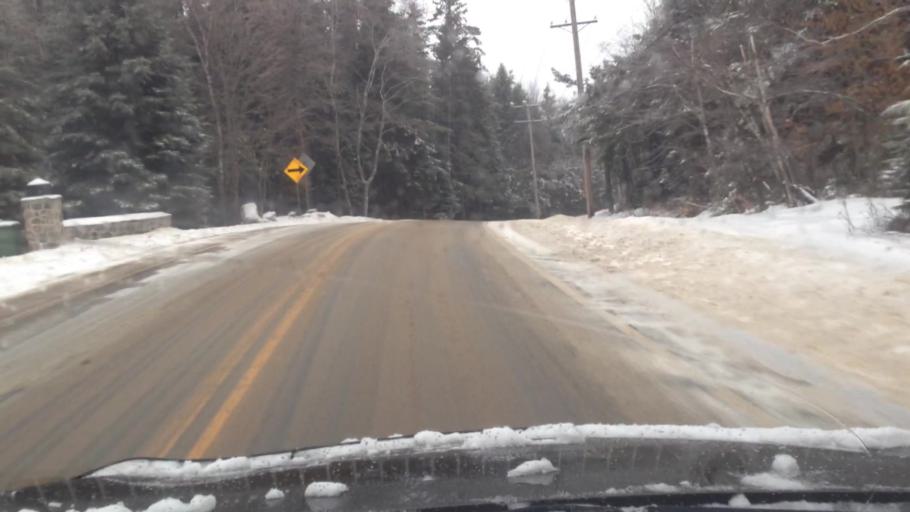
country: CA
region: Quebec
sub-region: Laurentides
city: Mont-Tremblant
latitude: 46.0273
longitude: -74.6043
